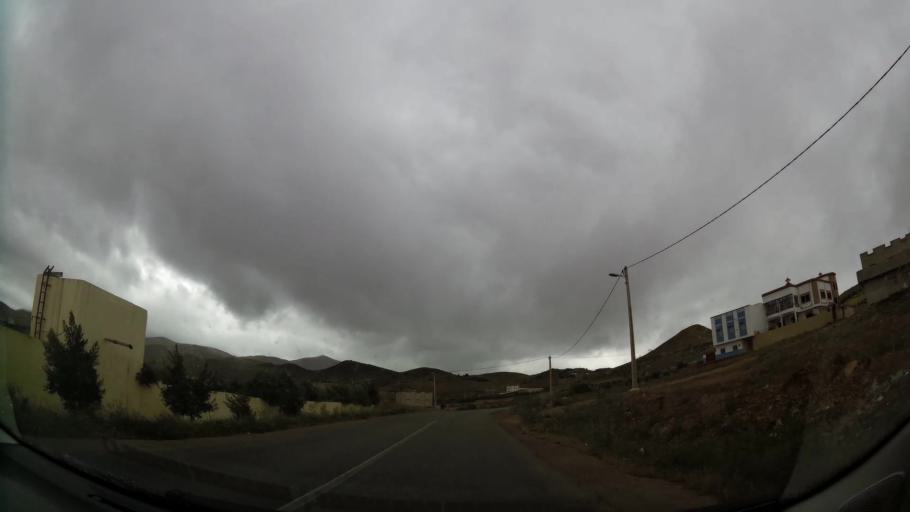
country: MA
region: Oriental
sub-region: Nador
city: Midar
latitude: 35.0594
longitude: -3.4683
